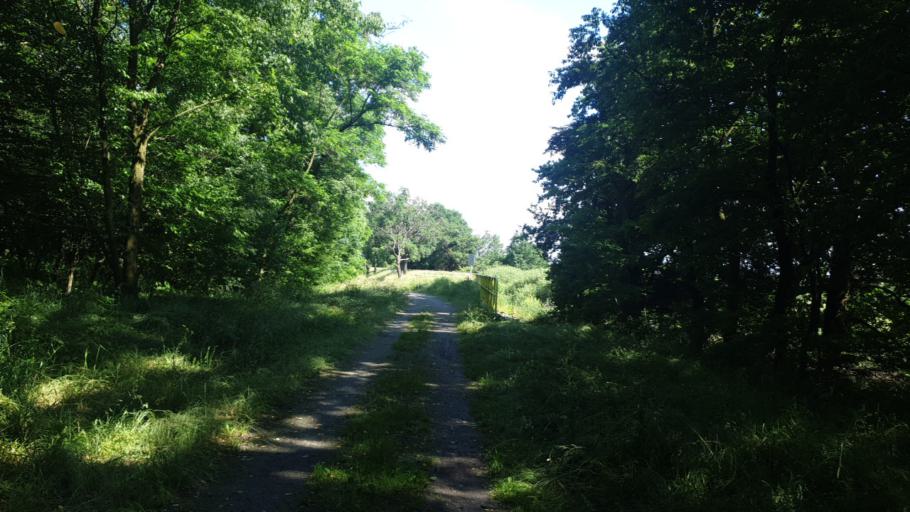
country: PL
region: Lower Silesian Voivodeship
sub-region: Powiat wroclawski
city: Radwanice
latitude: 51.0845
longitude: 17.1182
